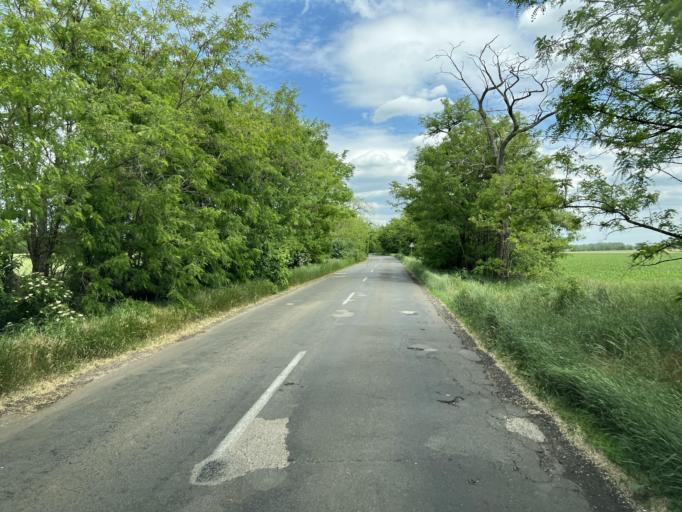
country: HU
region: Pest
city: Forropuszta
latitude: 47.4795
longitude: 19.6333
